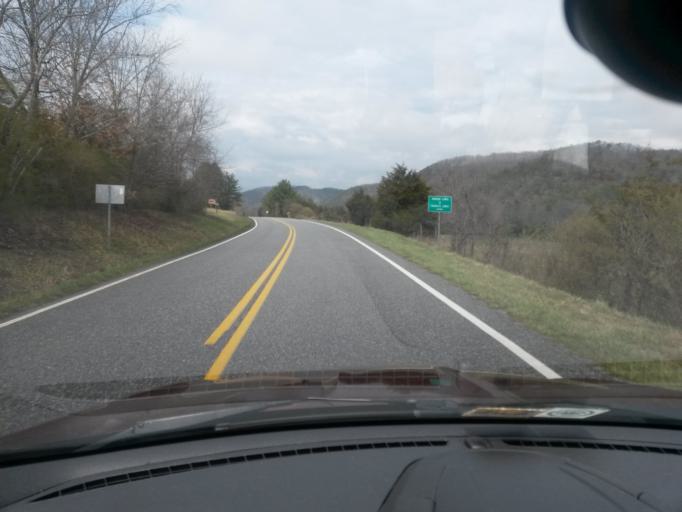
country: US
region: Virginia
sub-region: Bath County
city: Warm Springs
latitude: 38.0200
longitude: -79.6431
